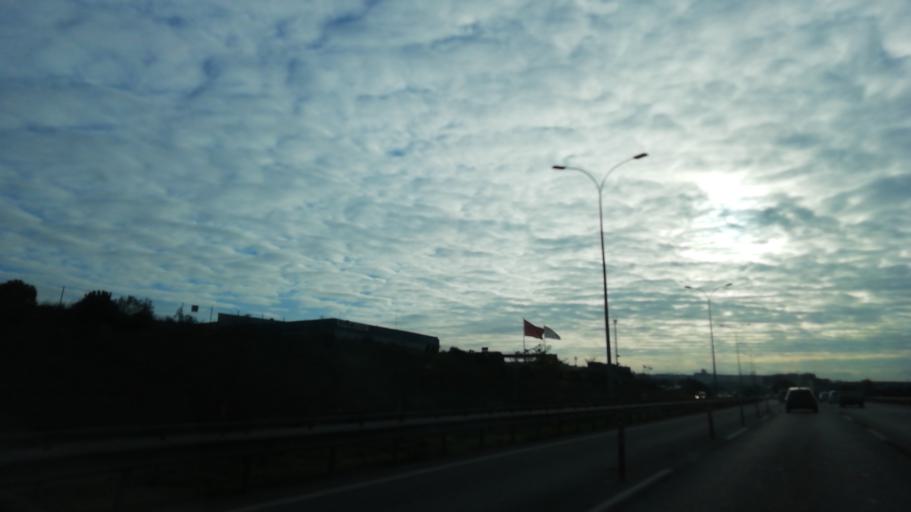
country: TR
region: Kocaeli
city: Balcik
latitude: 40.8820
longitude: 29.3797
